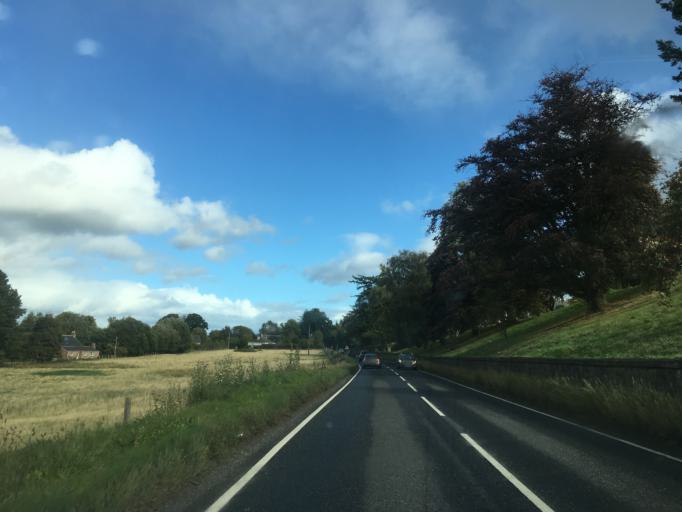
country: GB
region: Scotland
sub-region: Highland
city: Beauly
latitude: 57.4787
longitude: -4.3666
